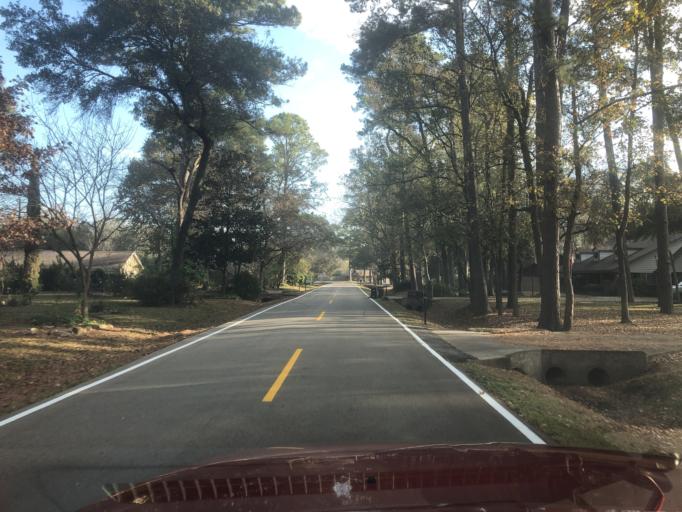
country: US
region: Texas
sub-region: Harris County
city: Spring
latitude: 30.0102
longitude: -95.4741
